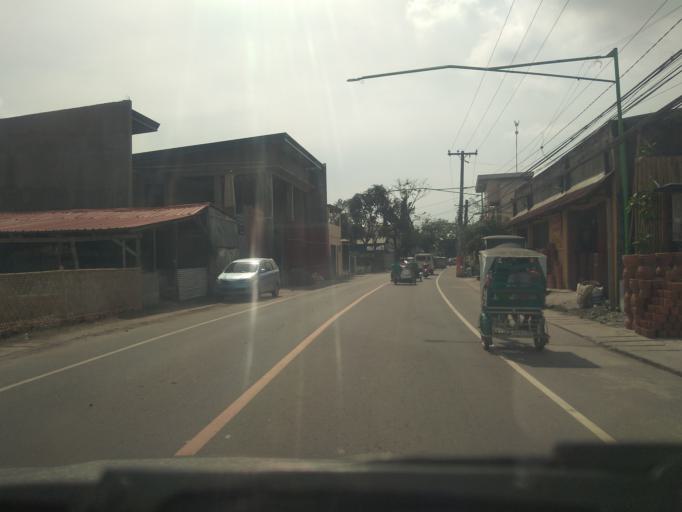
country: PH
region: Central Luzon
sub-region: Province of Pampanga
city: Pau
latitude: 15.0066
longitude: 120.7100
